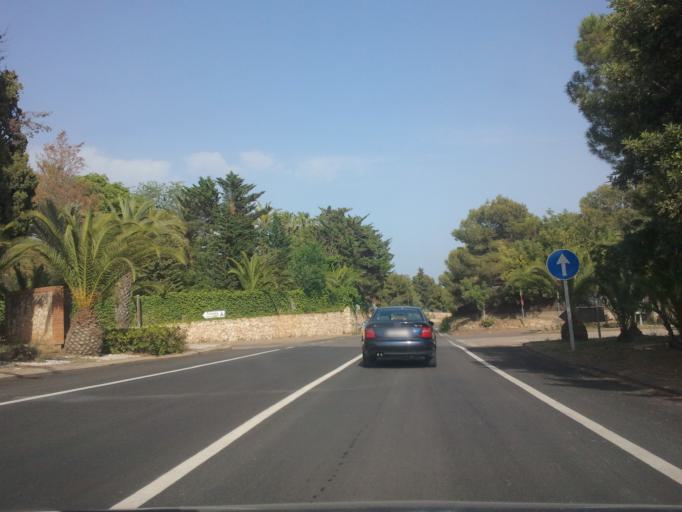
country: ES
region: Catalonia
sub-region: Provincia de Barcelona
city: Cubelles
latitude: 41.2316
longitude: 1.6906
